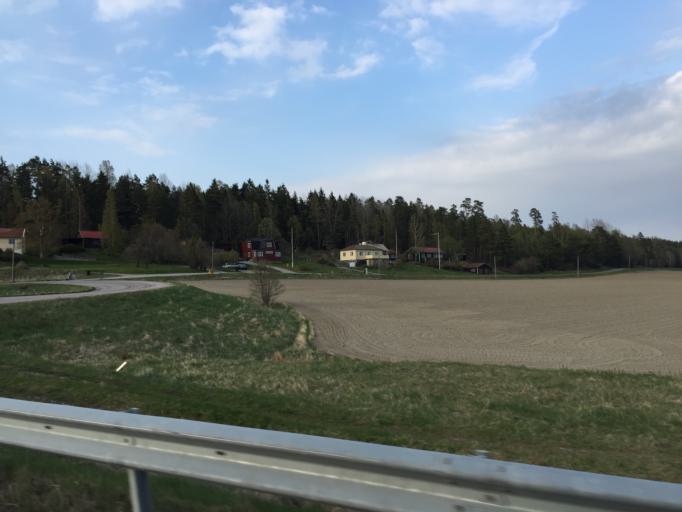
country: SE
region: Soedermanland
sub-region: Trosa Kommun
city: Vagnharad
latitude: 59.0178
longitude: 17.5916
